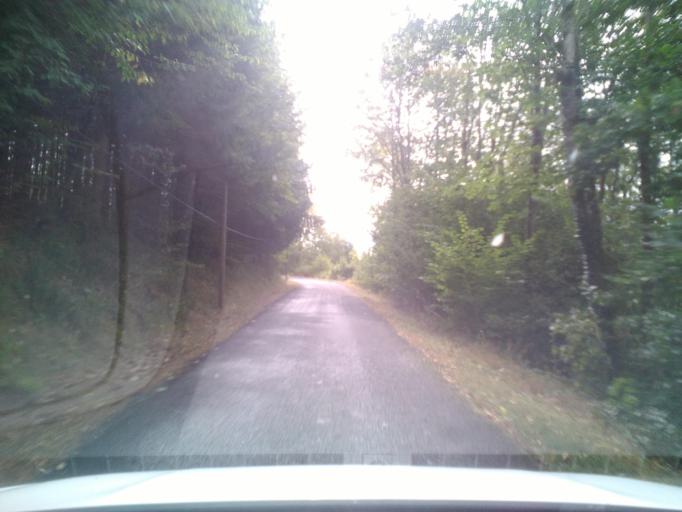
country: FR
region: Lorraine
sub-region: Departement des Vosges
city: Senones
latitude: 48.3616
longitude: 7.0045
